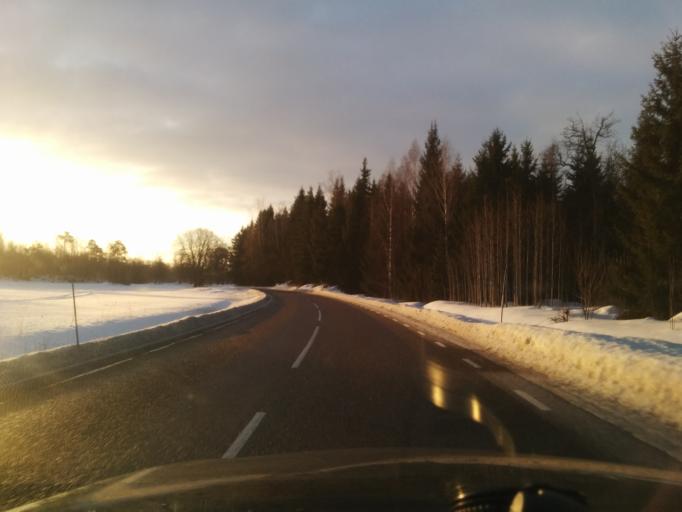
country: SE
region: Uppsala
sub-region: Tierps Kommun
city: Orbyhus
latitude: 60.2061
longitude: 17.6985
